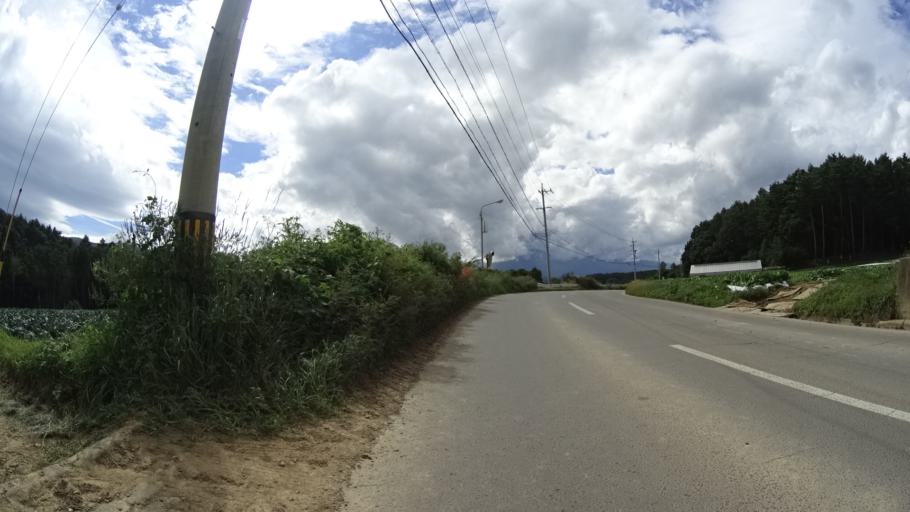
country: JP
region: Nagano
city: Saku
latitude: 35.9643
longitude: 138.5286
